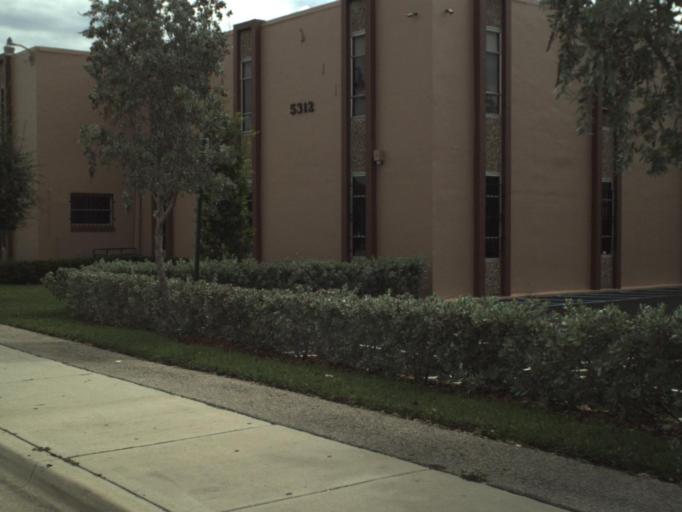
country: US
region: Florida
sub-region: Palm Beach County
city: Riviera Beach
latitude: 26.7583
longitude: -80.0556
